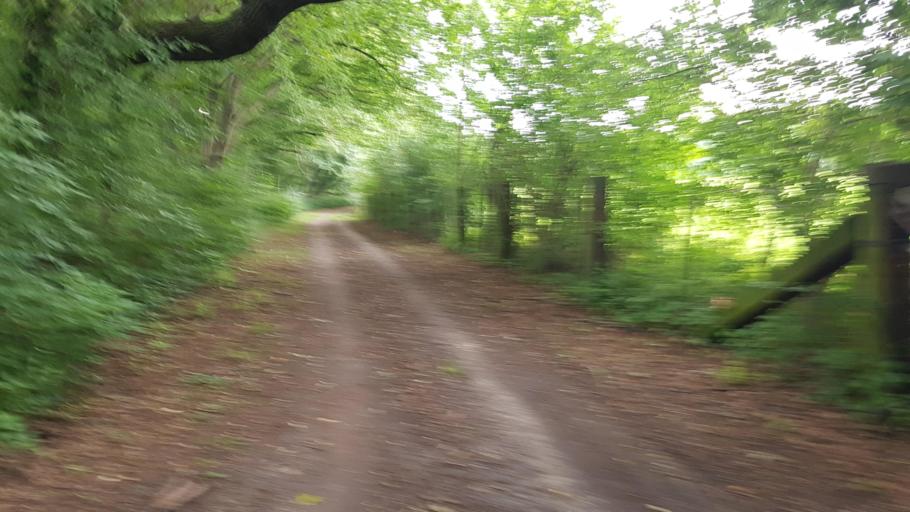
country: DE
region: Brandenburg
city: Sonnewalde
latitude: 51.6971
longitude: 13.6347
